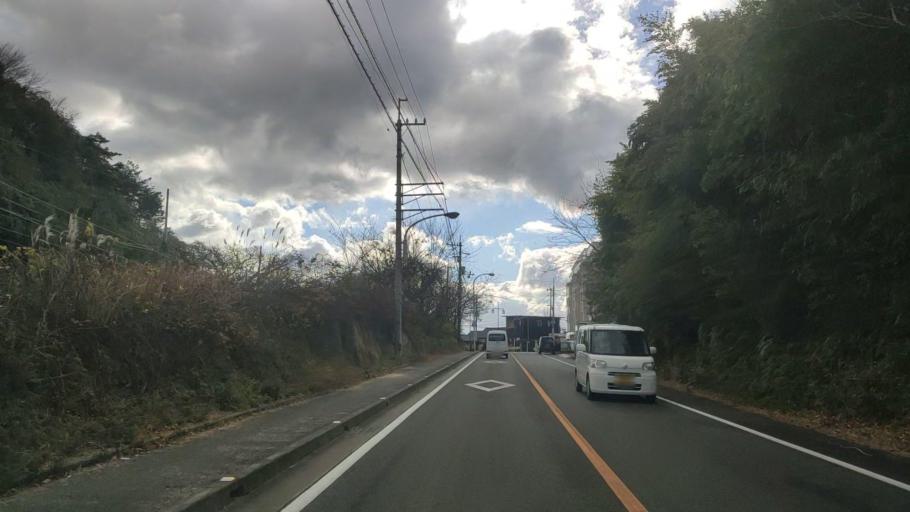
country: JP
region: Ehime
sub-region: Shikoku-chuo Shi
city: Matsuyama
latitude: 33.8787
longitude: 132.7034
